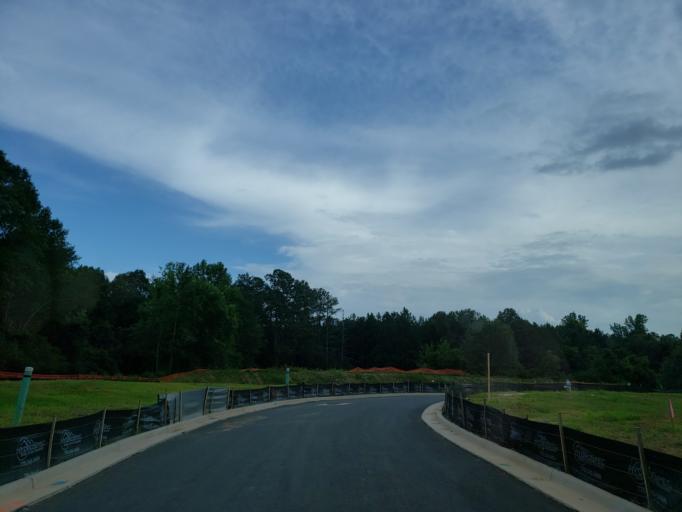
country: US
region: Georgia
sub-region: Cherokee County
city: Ball Ground
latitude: 34.2417
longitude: -84.3496
